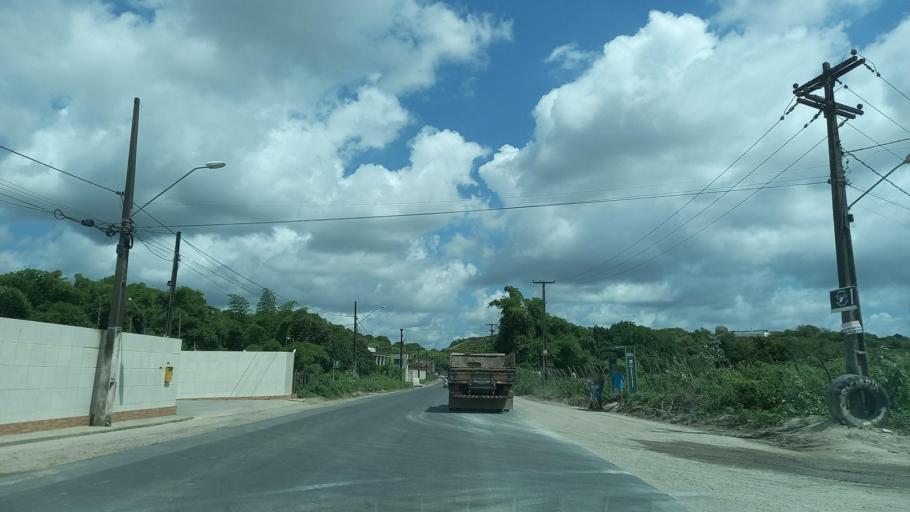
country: BR
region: Pernambuco
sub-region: Jaboatao Dos Guararapes
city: Jaboatao dos Guararapes
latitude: -8.1235
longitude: -35.0062
